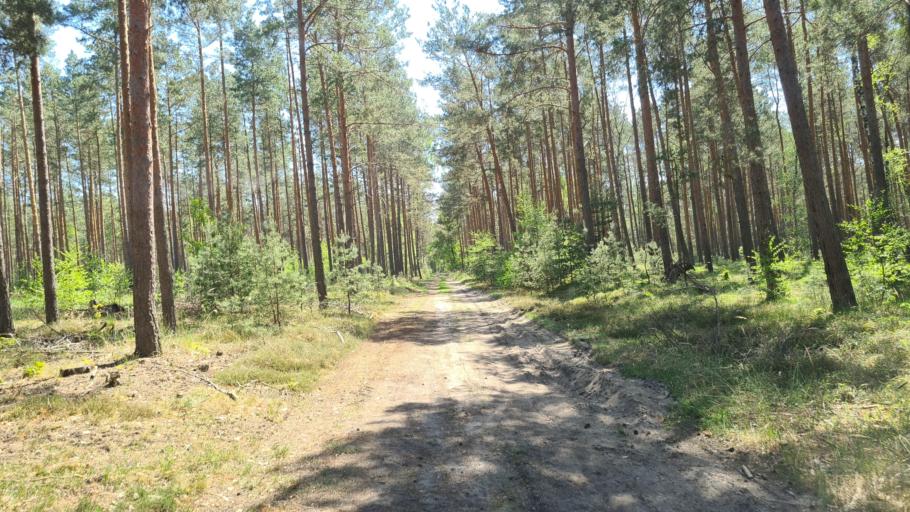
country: DE
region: Brandenburg
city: Sallgast
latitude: 51.5873
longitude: 13.8755
